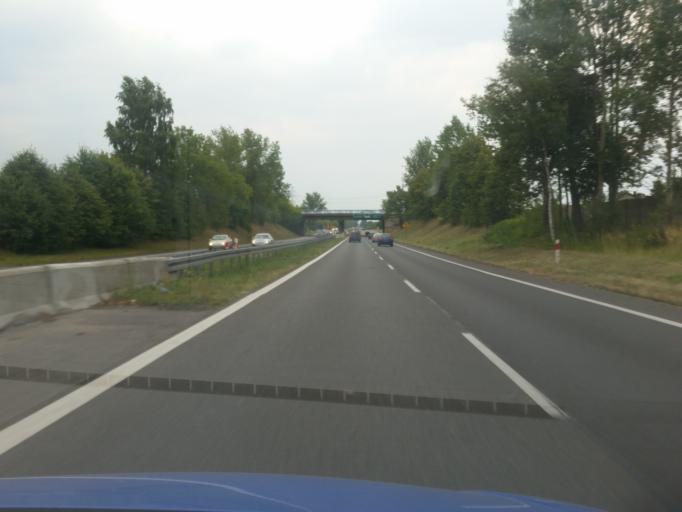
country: PL
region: Silesian Voivodeship
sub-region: Powiat bedzinski
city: Bedzin
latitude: 50.3370
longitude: 19.1103
